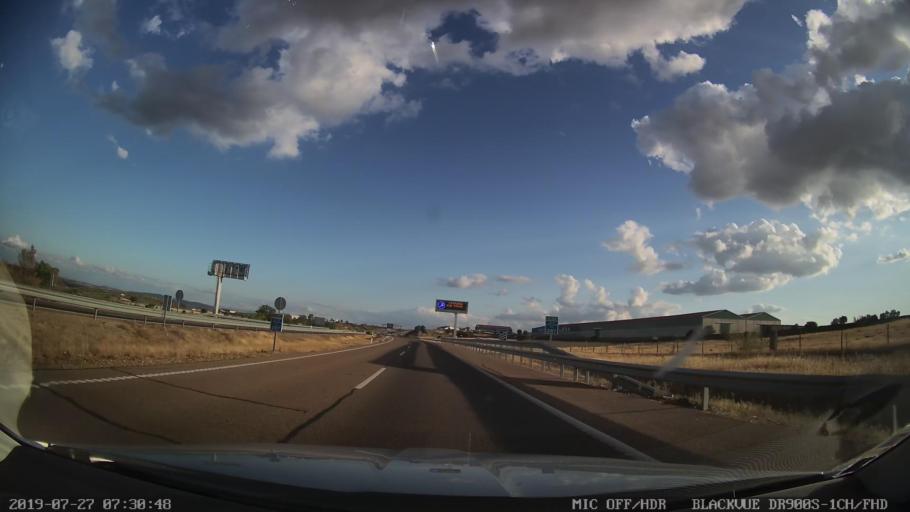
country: ES
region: Extremadura
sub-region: Provincia de Caceres
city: Escurial
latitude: 39.1824
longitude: -5.8962
